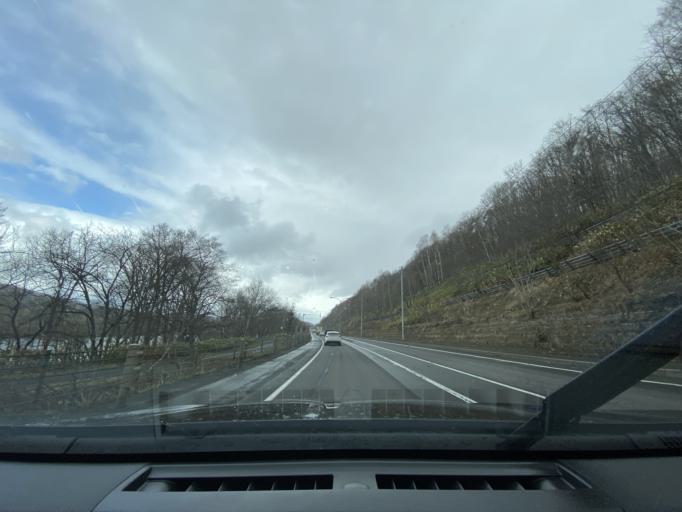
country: JP
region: Hokkaido
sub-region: Asahikawa-shi
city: Asahikawa
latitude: 43.7552
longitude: 142.2739
